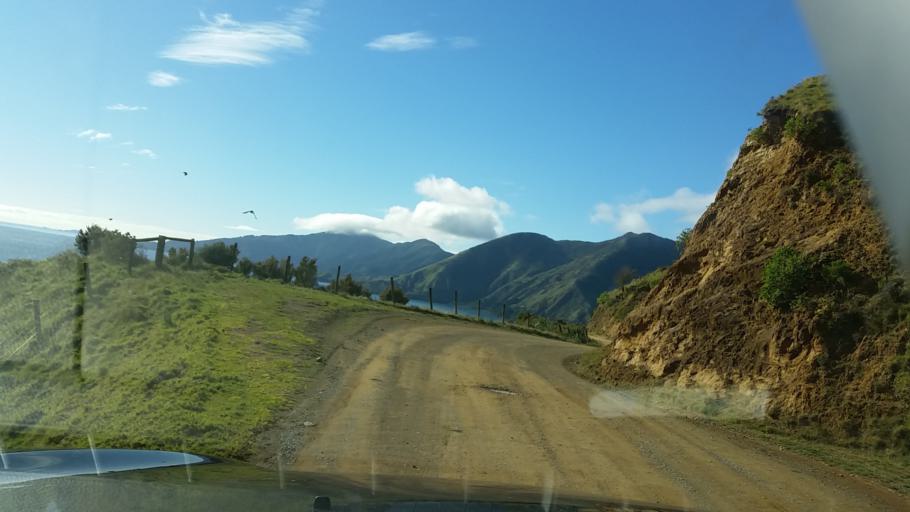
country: NZ
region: Marlborough
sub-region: Marlborough District
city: Picton
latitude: -40.9848
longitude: 173.8319
